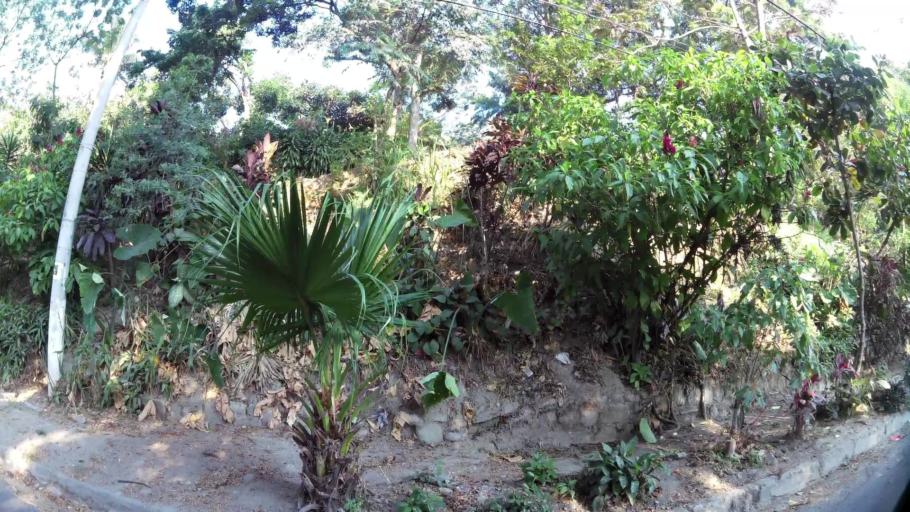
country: SV
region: San Salvador
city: San Salvador
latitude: 13.6786
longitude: -89.2019
